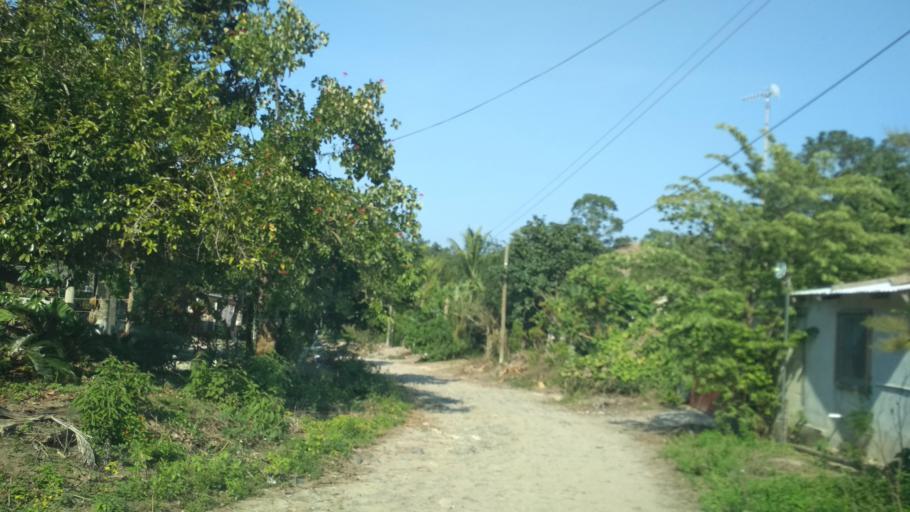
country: MX
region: Puebla
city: San Jose Acateno
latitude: 20.1848
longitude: -97.2611
